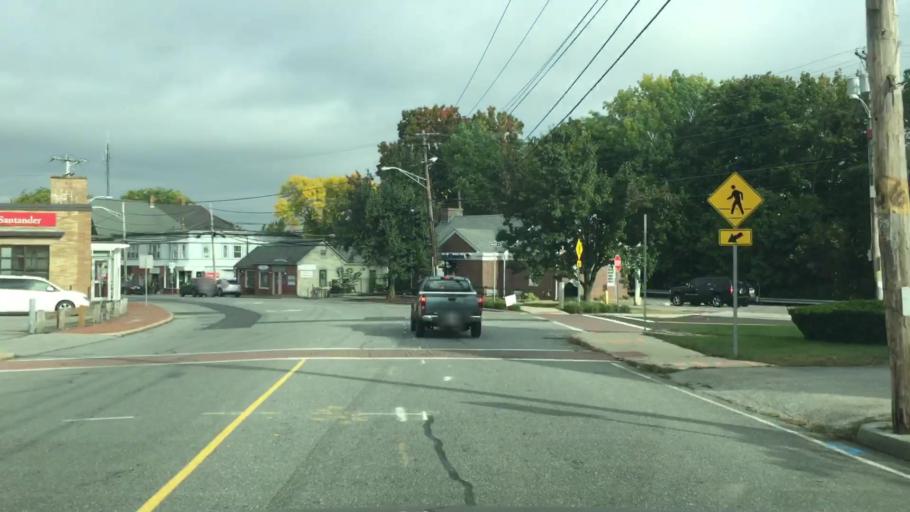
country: US
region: Massachusetts
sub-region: Essex County
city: North Andover
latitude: 42.7016
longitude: -71.1297
